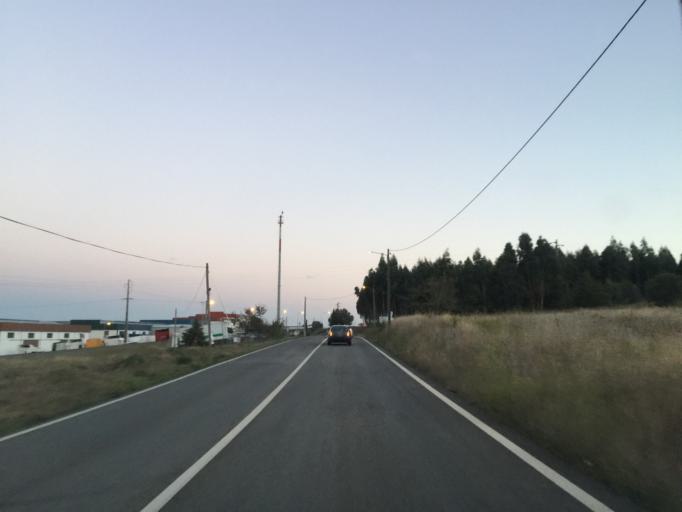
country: PT
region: Lisbon
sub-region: Alenquer
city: Alenquer
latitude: 39.1296
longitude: -8.9941
